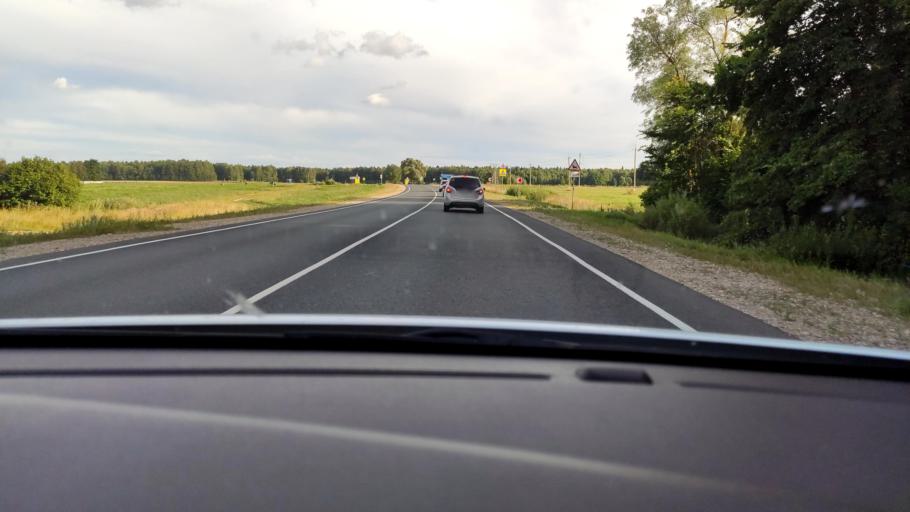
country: RU
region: Mariy-El
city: Krasnogorskiy
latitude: 56.1951
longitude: 48.2365
